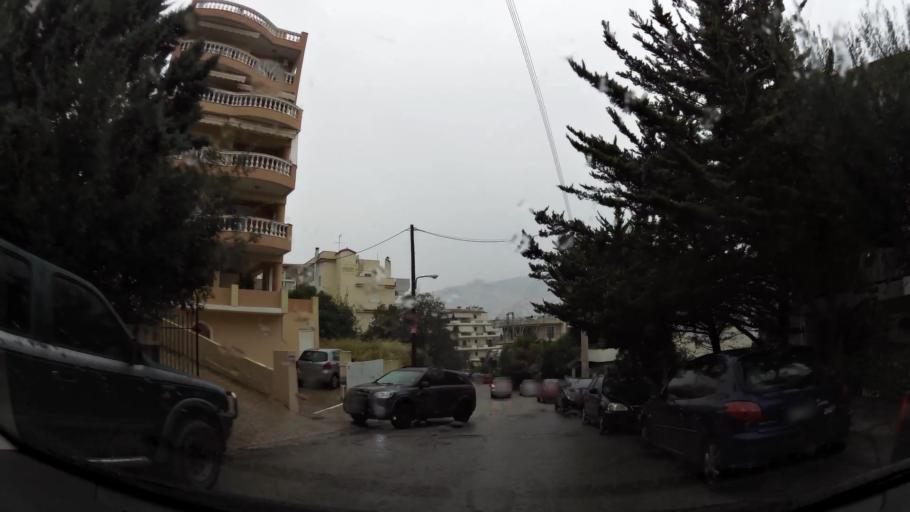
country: GR
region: Attica
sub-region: Nomarchia Athinas
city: Chaidari
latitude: 38.0103
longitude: 23.6586
